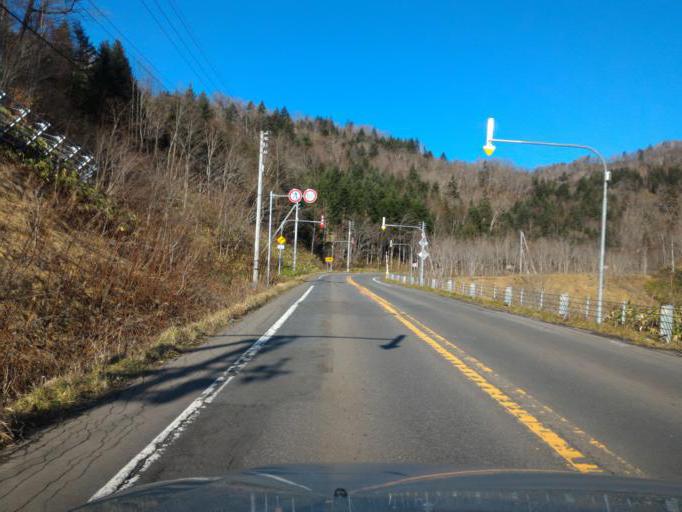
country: JP
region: Hokkaido
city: Bibai
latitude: 43.2825
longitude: 142.0633
